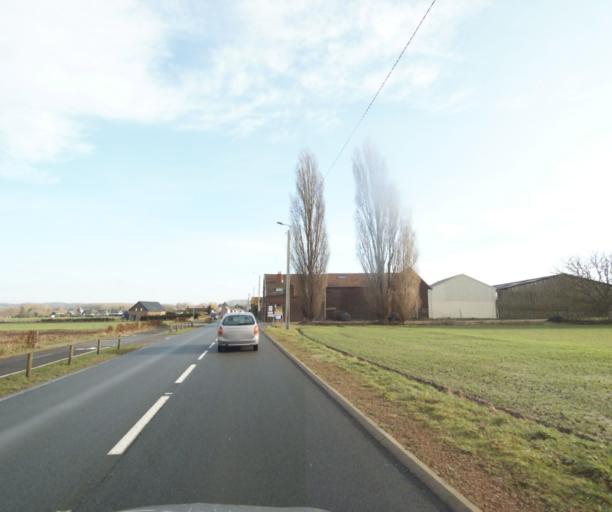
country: FR
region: Nord-Pas-de-Calais
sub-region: Departement du Nord
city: Thiant
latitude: 50.3041
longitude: 3.4640
